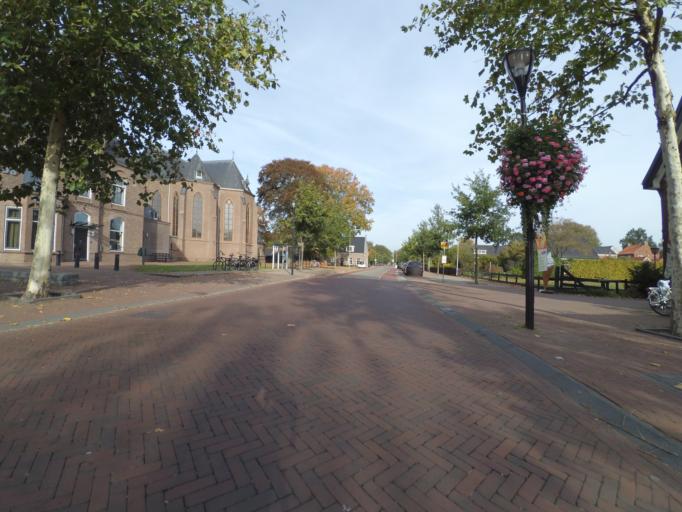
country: NL
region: Overijssel
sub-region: Gemeente Raalte
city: Raalte
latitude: 52.3329
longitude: 6.2810
